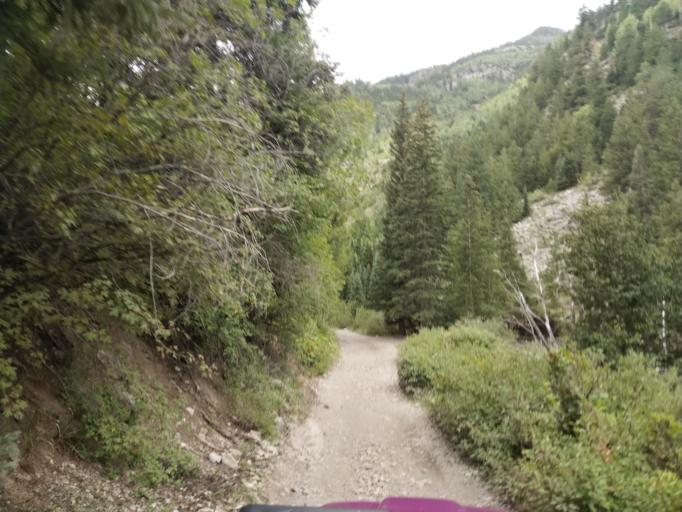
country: US
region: Colorado
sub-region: Gunnison County
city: Crested Butte
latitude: 39.0569
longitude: -107.1341
